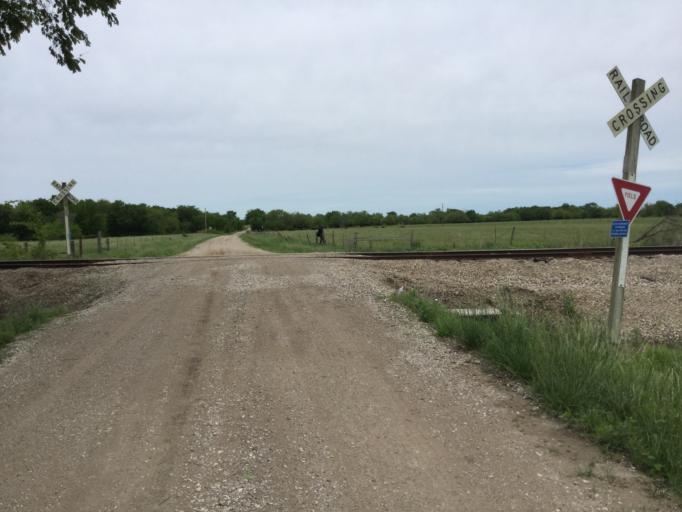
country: US
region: Kansas
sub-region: Labette County
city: Altamont
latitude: 37.1772
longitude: -95.2312
